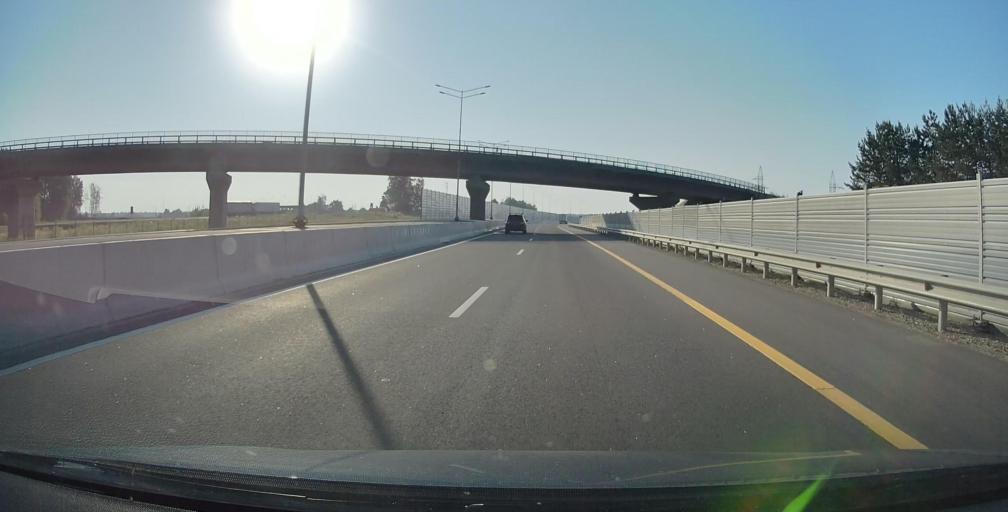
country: RU
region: Moskovskaya
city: Podosinki
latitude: 56.1846
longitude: 37.6080
